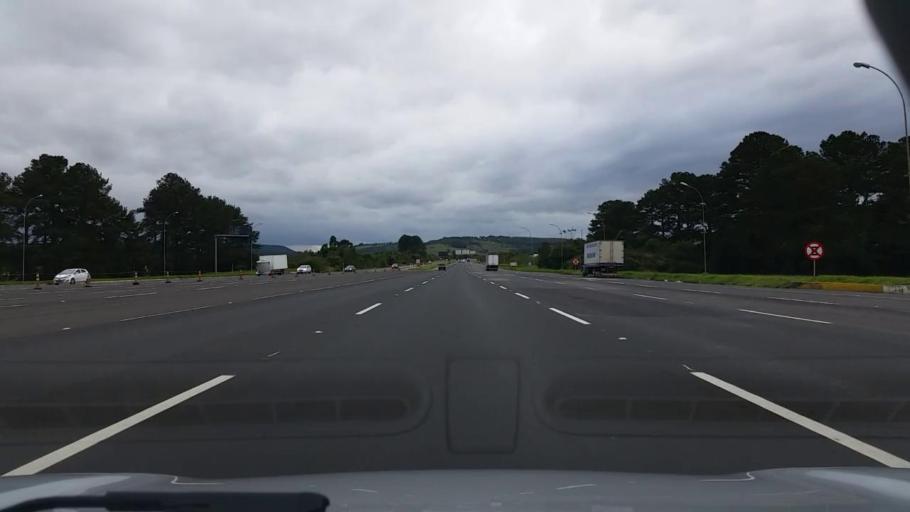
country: BR
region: Rio Grande do Sul
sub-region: Osorio
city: Osorio
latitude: -29.8859
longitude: -50.4497
